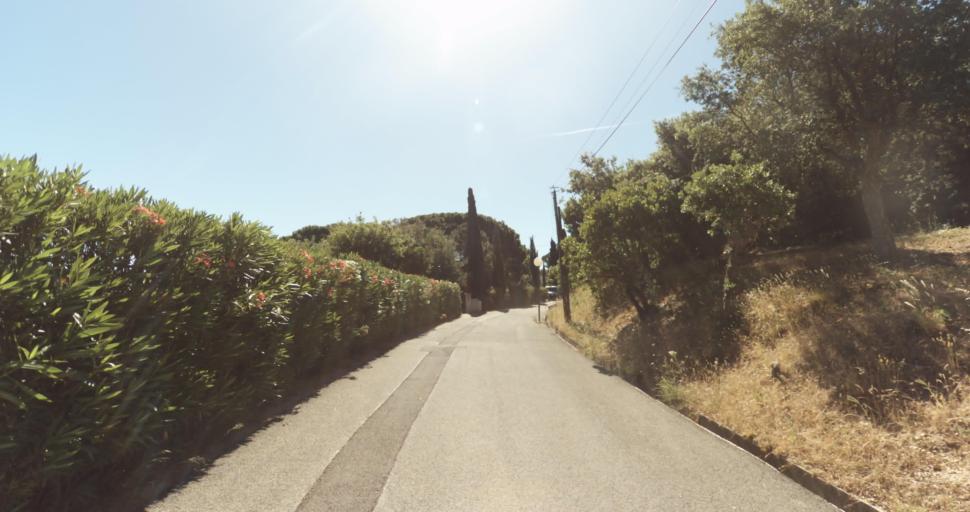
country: FR
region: Provence-Alpes-Cote d'Azur
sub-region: Departement du Var
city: Saint-Tropez
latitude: 43.2604
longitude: 6.6122
